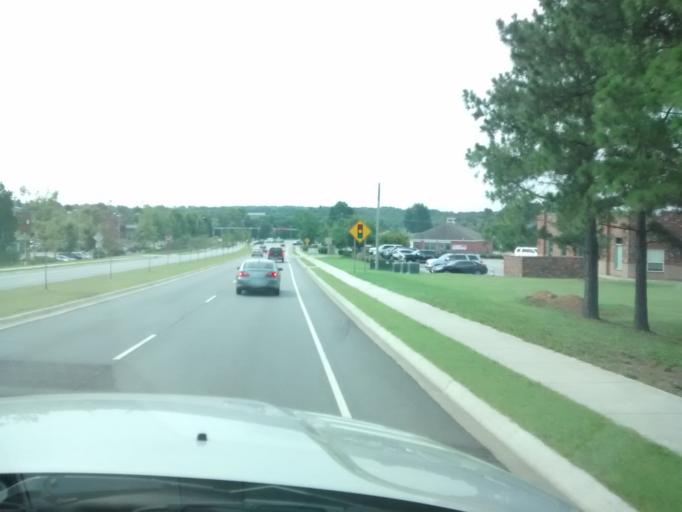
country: US
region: Arkansas
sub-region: Washington County
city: Johnson
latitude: 36.1222
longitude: -94.1202
